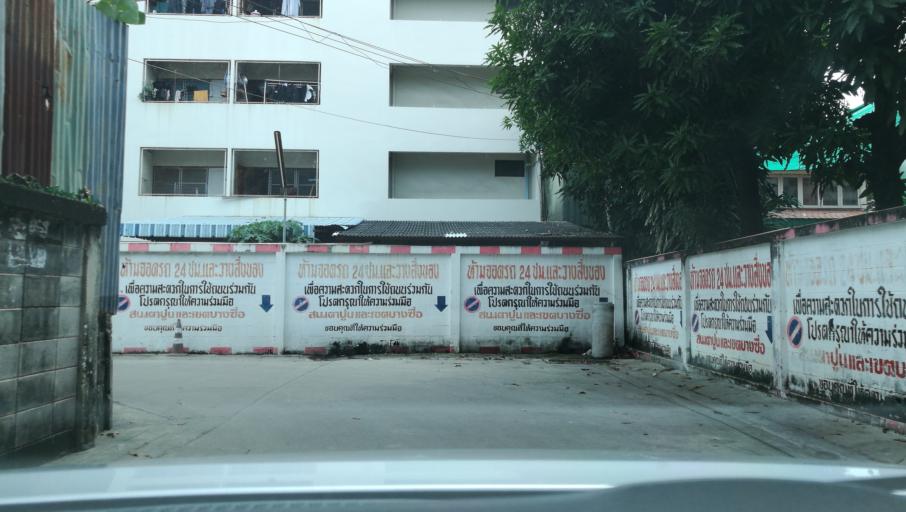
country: TH
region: Bangkok
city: Bang Sue
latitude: 13.8123
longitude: 100.5323
